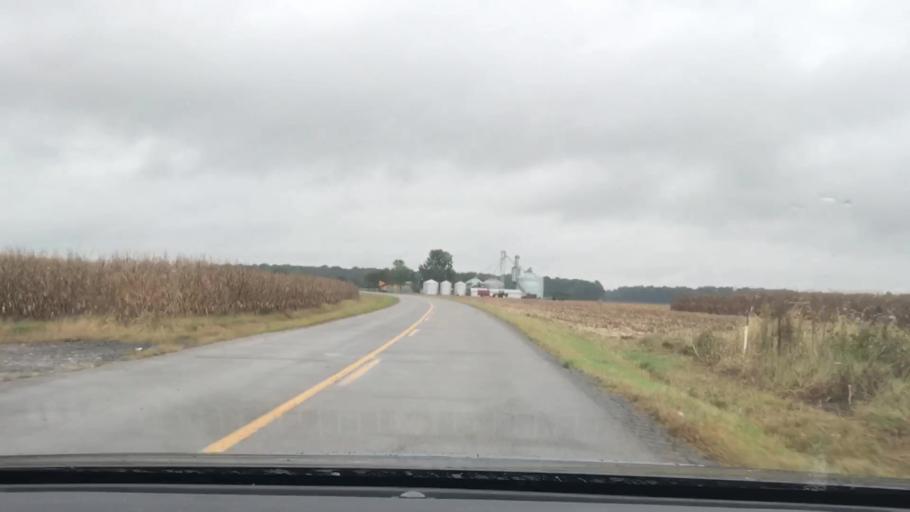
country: US
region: Kentucky
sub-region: McLean County
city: Calhoun
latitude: 37.5265
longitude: -87.3388
